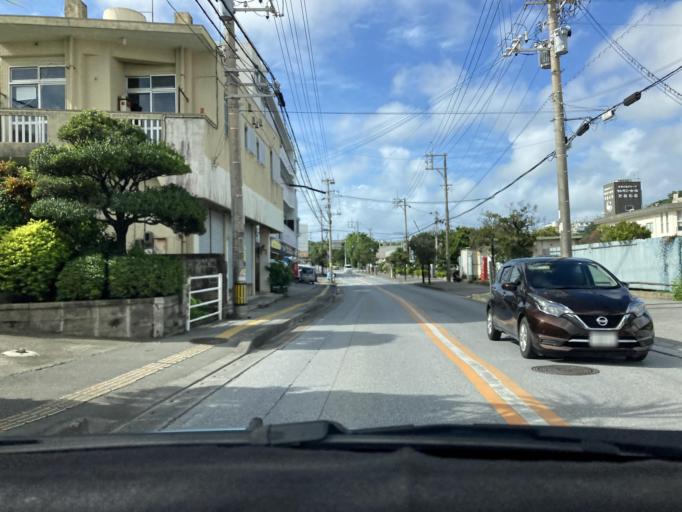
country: JP
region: Okinawa
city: Tomigusuku
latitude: 26.1846
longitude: 127.6866
